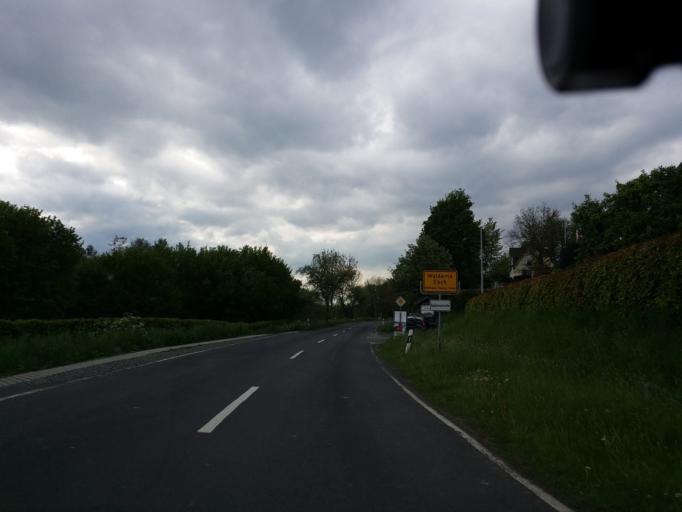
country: DE
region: Hesse
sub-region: Regierungsbezirk Darmstadt
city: Waldems
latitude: 50.2467
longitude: 8.3216
